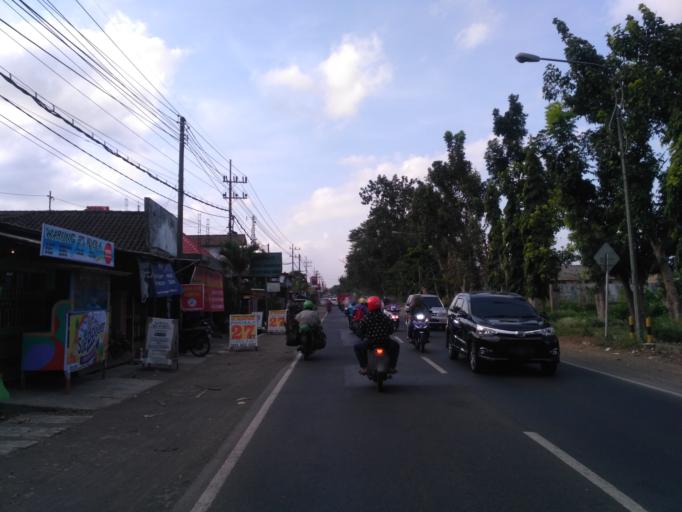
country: ID
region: East Java
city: Pakisaji
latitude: -8.0575
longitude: 112.6028
